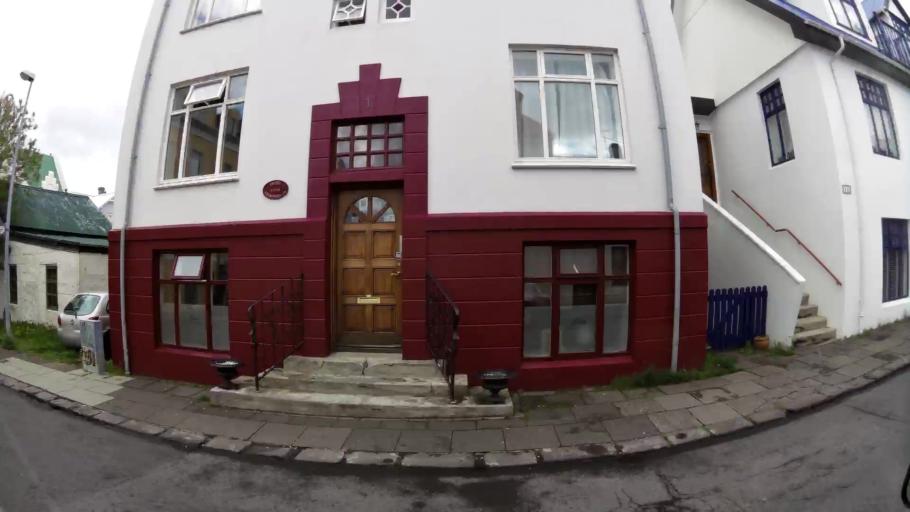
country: IS
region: Capital Region
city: Kopavogur
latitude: 64.1448
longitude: -21.9347
